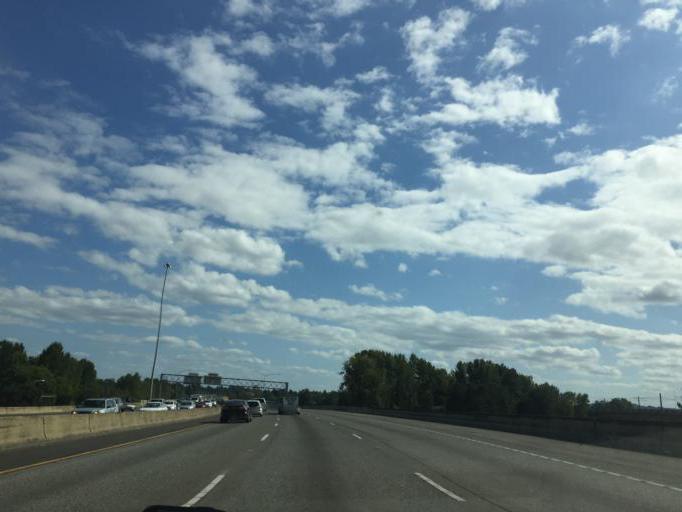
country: US
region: Washington
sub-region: Clark County
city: Vancouver
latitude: 45.5964
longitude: -122.6846
